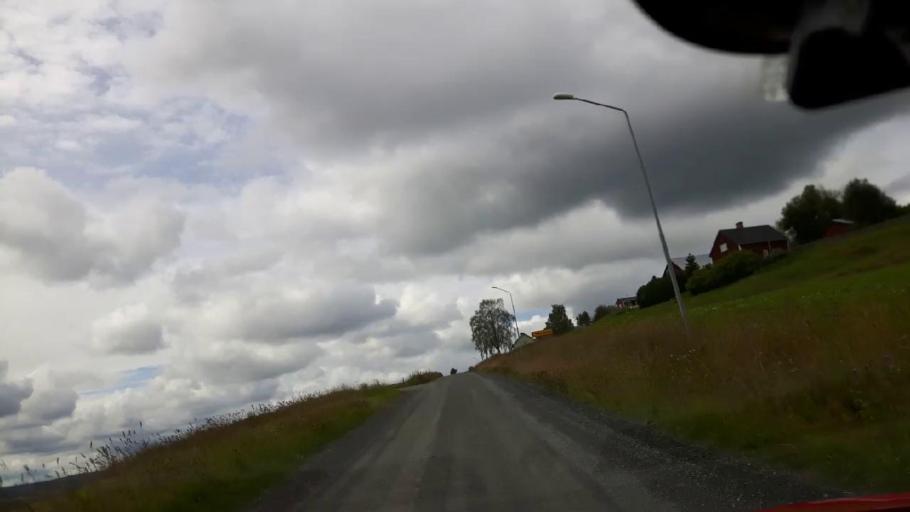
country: SE
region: Jaemtland
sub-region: Krokoms Kommun
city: Valla
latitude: 63.4878
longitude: 13.9955
